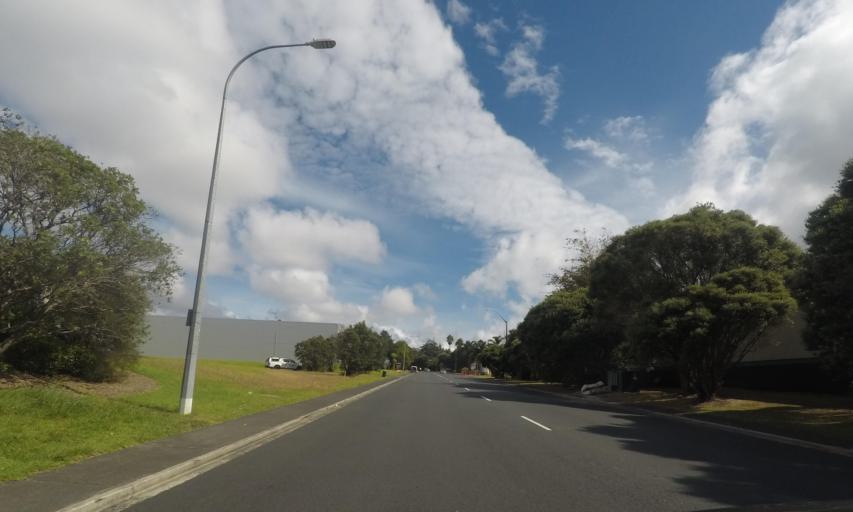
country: NZ
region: Auckland
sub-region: Auckland
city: Rothesay Bay
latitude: -36.7503
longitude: 174.7007
